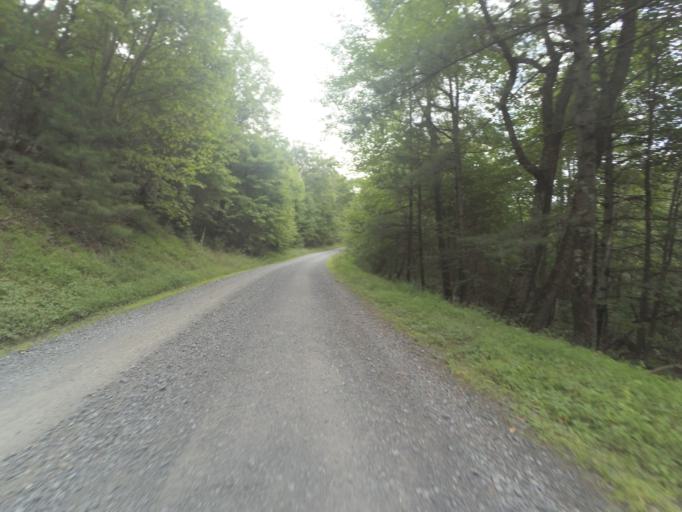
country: US
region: Pennsylvania
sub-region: Centre County
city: Boalsburg
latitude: 40.7149
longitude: -77.7633
